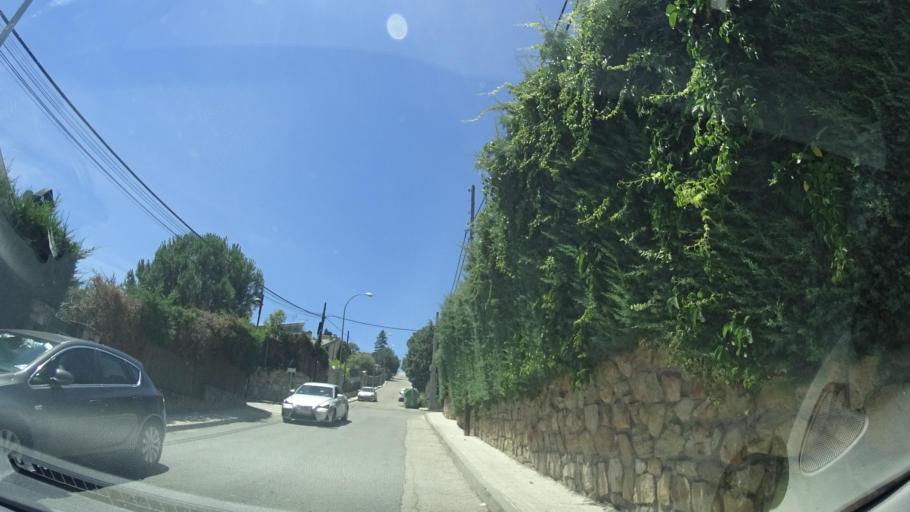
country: ES
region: Madrid
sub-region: Provincia de Madrid
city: Galapagar
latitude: 40.5946
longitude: -3.9878
